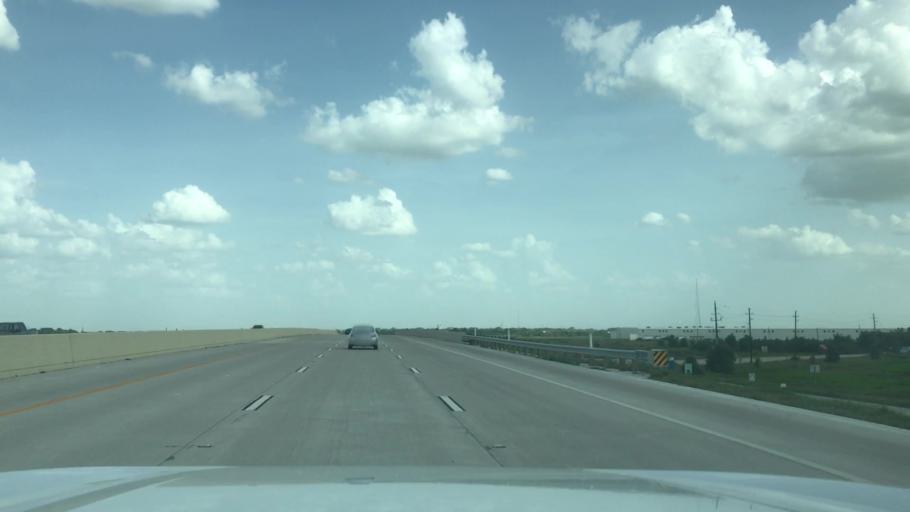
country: US
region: Texas
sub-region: Waller County
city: Waller
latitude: 30.0485
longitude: -95.8755
